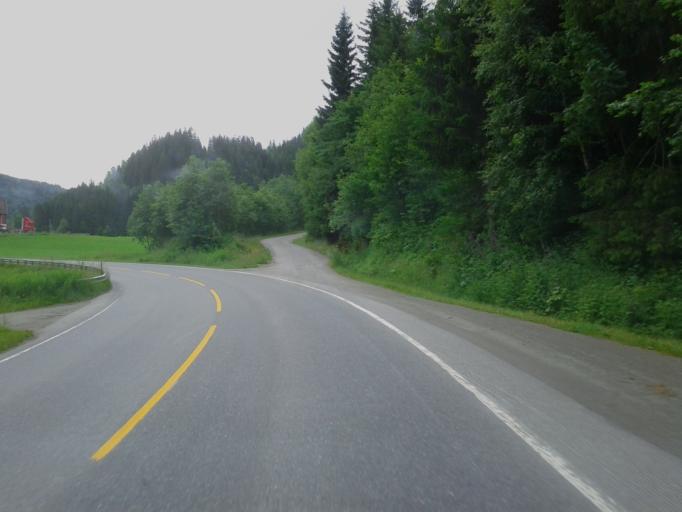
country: NO
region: Sor-Trondelag
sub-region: Midtre Gauldal
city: Storen
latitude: 63.0148
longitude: 10.4334
